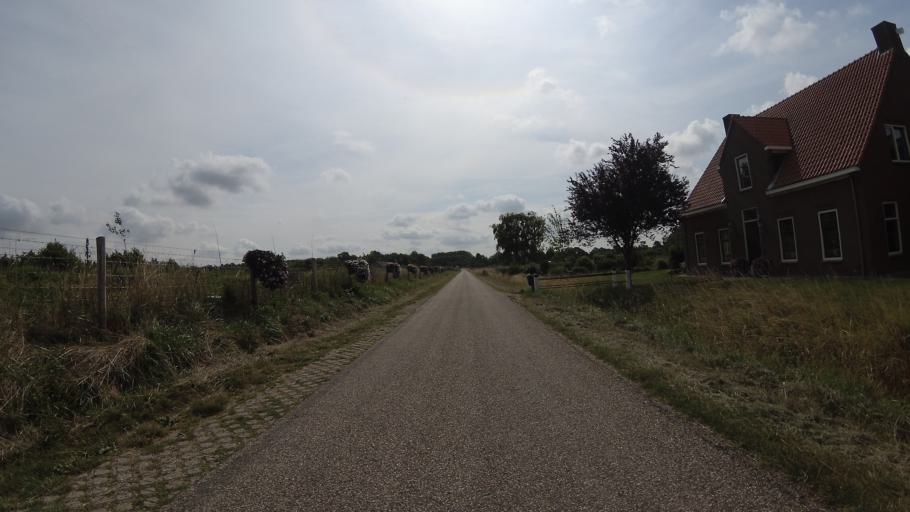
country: NL
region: Zeeland
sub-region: Gemeente Noord-Beveland
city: Kamperland
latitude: 51.5651
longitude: 3.6870
